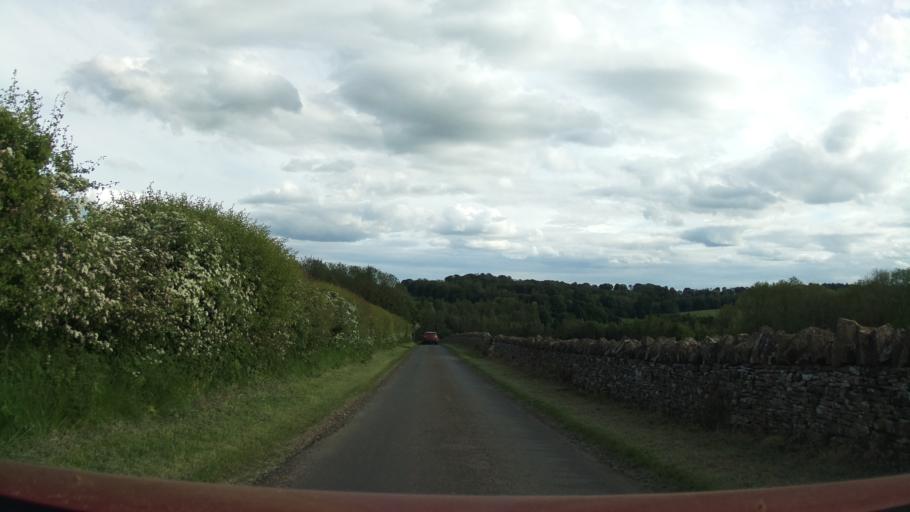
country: GB
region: England
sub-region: Gloucestershire
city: Westfield
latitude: 51.8869
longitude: -1.8885
